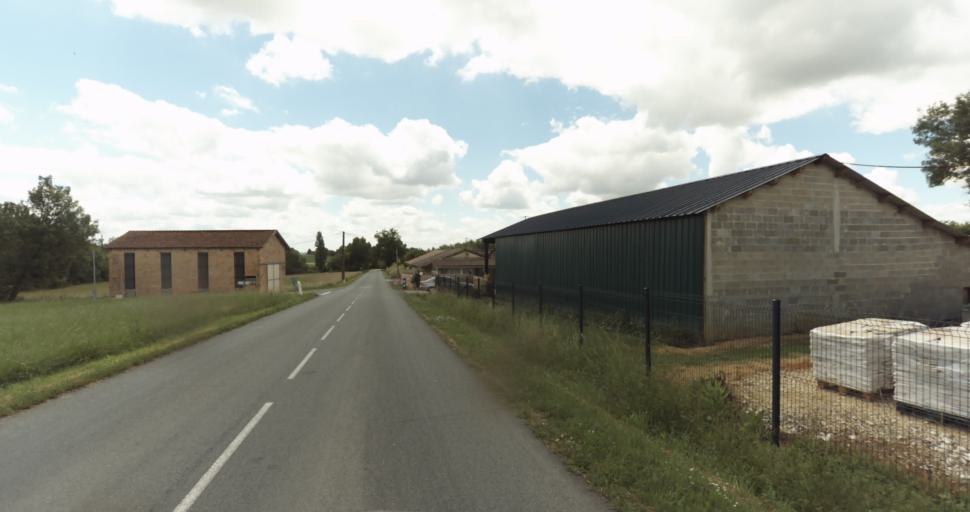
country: FR
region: Aquitaine
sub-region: Departement de la Dordogne
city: Beaumont-du-Perigord
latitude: 44.7059
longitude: 0.7500
